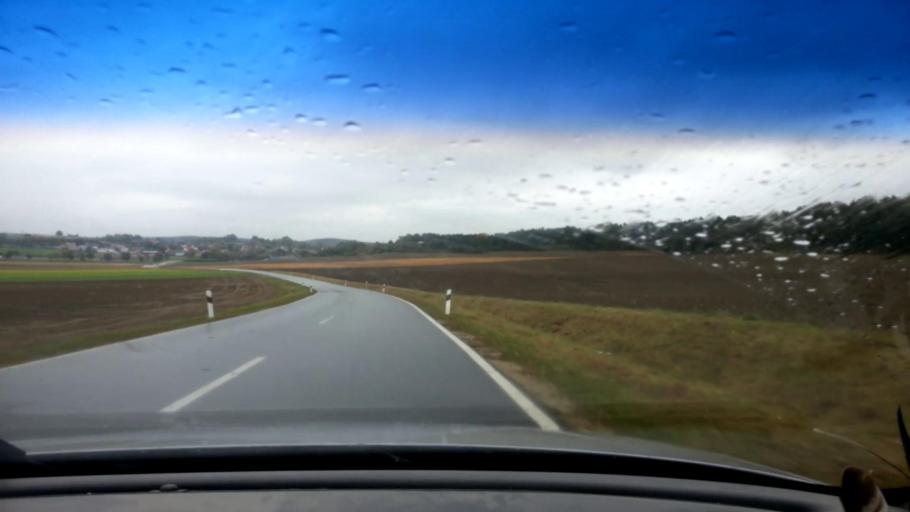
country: DE
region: Bavaria
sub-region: Upper Franconia
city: Konigsfeld
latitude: 49.9365
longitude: 11.1542
